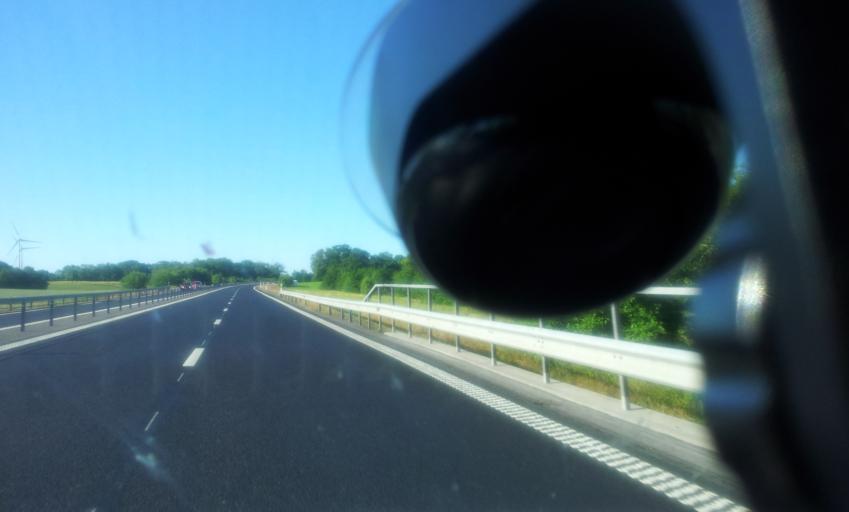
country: SE
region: Kalmar
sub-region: Torsas Kommun
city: Torsas
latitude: 56.4477
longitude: 16.0790
